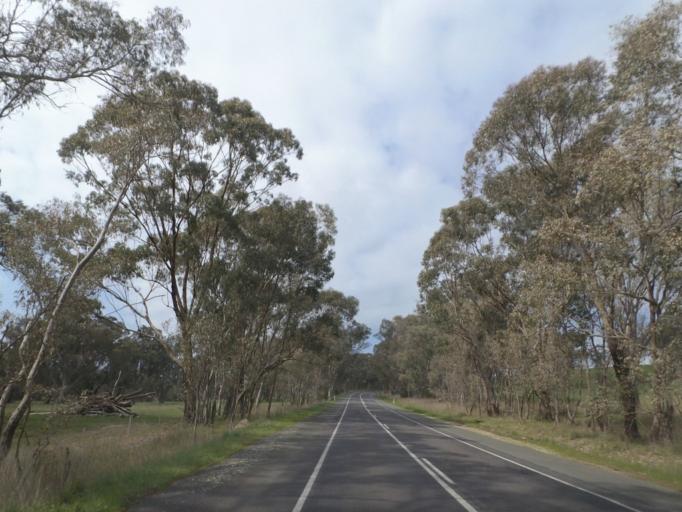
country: AU
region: Victoria
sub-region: Murrindindi
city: Kinglake West
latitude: -37.1582
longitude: 145.2881
